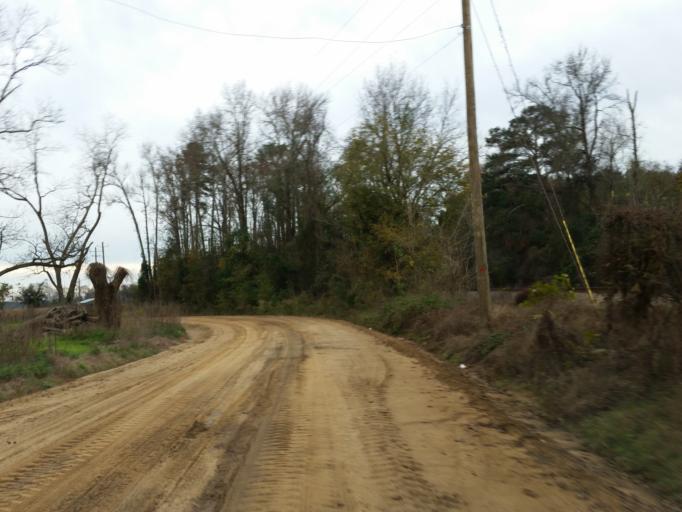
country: US
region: Georgia
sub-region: Dooly County
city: Vienna
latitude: 32.1518
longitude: -83.7722
